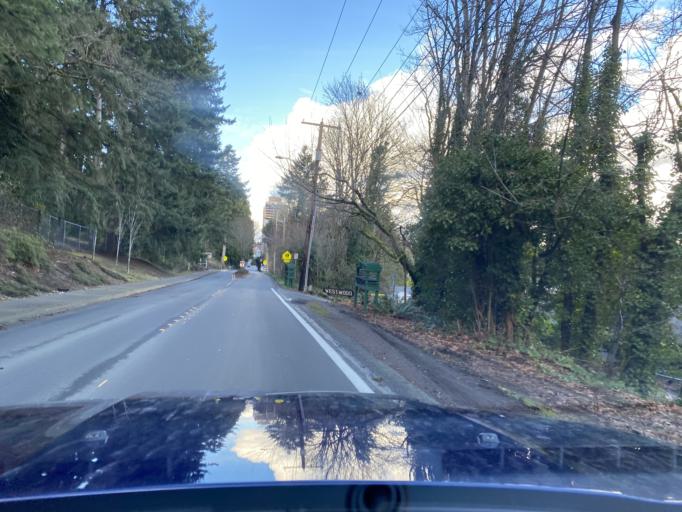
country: US
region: Washington
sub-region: King County
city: Bellevue
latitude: 47.6051
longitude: -122.1960
